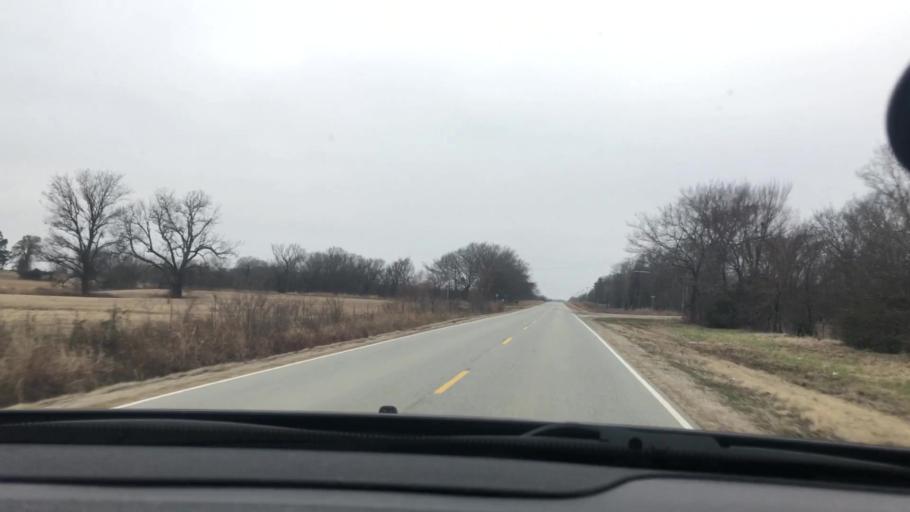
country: US
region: Oklahoma
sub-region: Coal County
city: Coalgate
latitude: 34.5285
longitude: -96.2654
